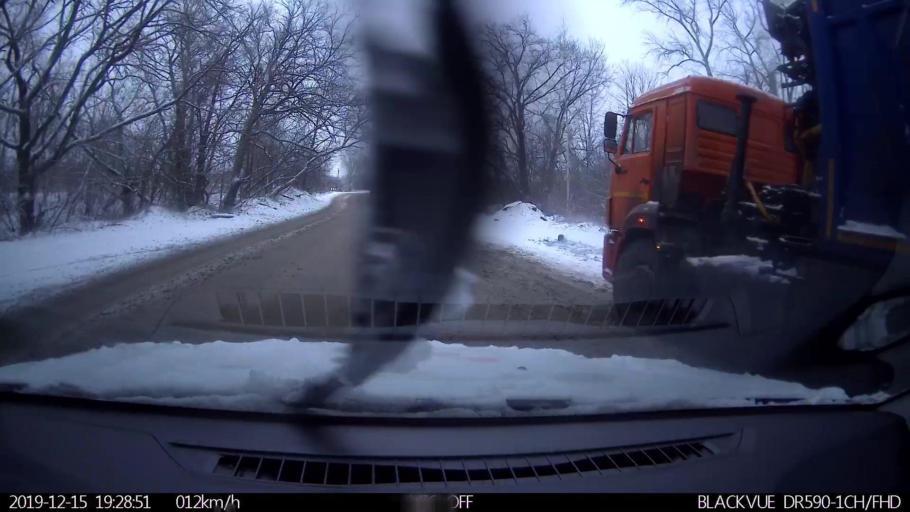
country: RU
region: Nizjnij Novgorod
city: Neklyudovo
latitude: 56.3571
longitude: 43.8913
